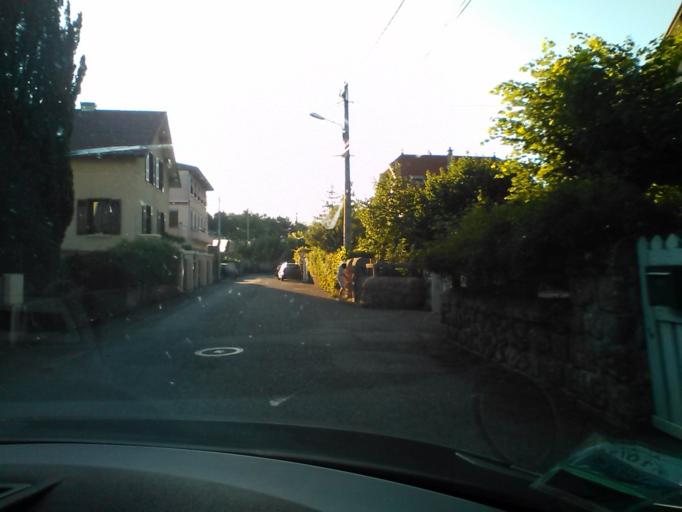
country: FR
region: Rhone-Alpes
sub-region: Departement de la Savoie
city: Chambery
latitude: 45.5643
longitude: 5.9487
